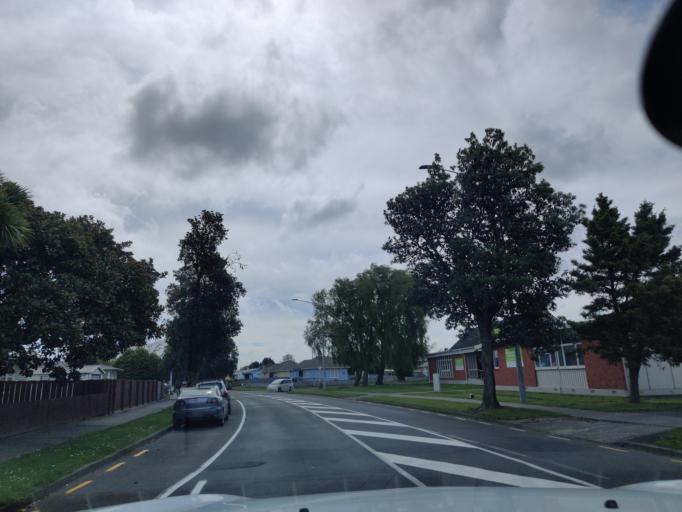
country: NZ
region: Manawatu-Wanganui
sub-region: Palmerston North City
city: Palmerston North
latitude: -40.3592
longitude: 175.5863
